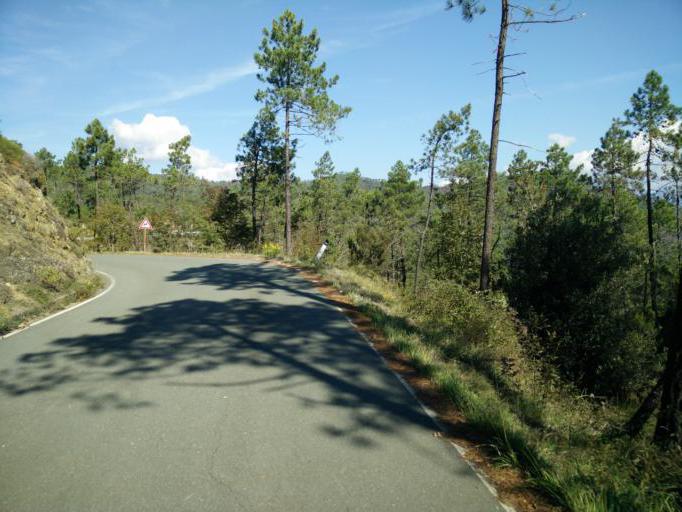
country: IT
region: Liguria
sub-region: Provincia di La Spezia
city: Framura
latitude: 44.2364
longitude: 9.5835
